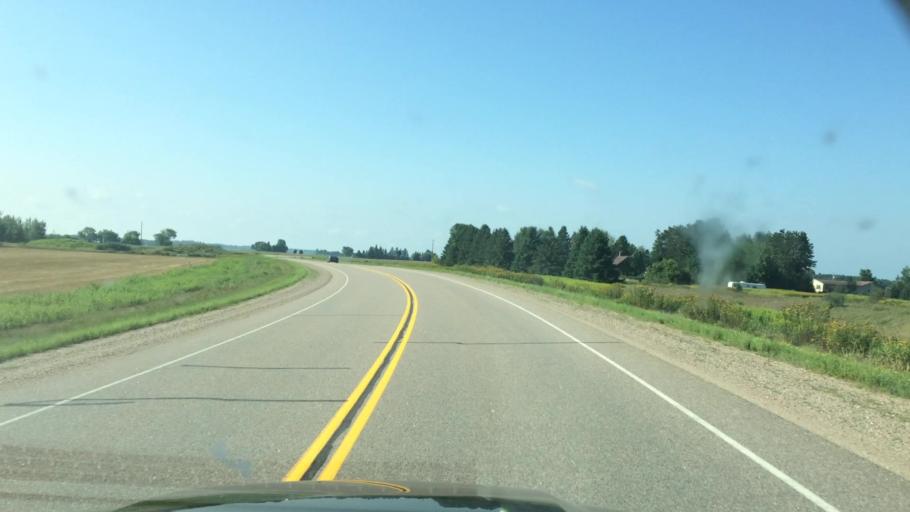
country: US
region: Wisconsin
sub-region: Langlade County
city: Antigo
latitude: 45.1497
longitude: -89.1844
